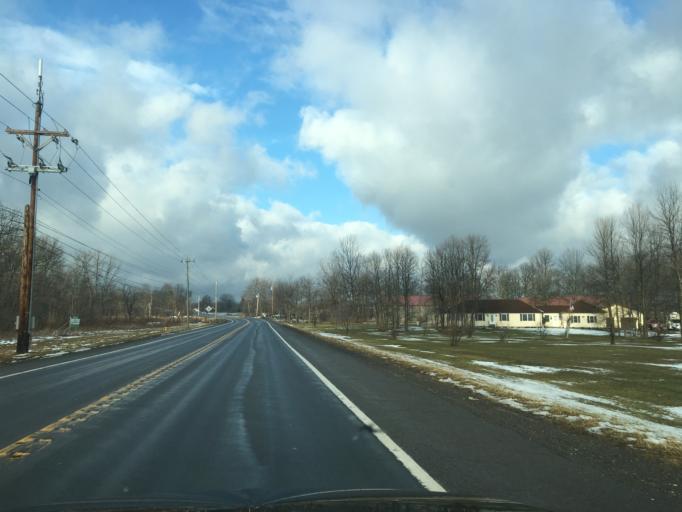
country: US
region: New York
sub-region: Ontario County
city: Victor
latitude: 42.9730
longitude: -77.3202
